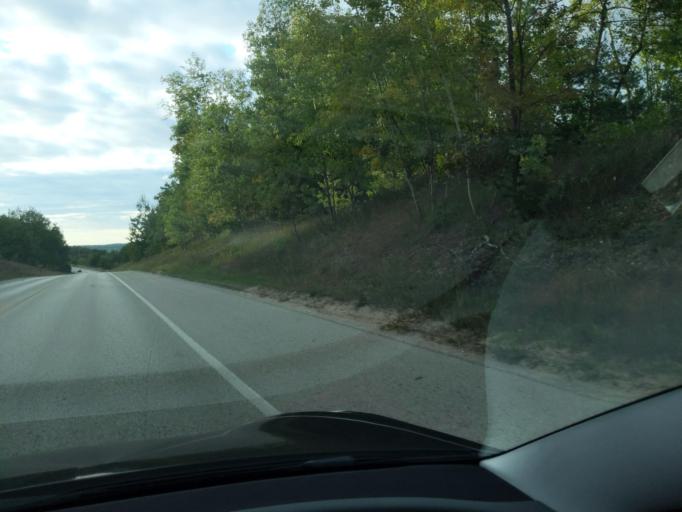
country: US
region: Michigan
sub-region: Kalkaska County
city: Rapid City
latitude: 44.7809
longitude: -85.2798
